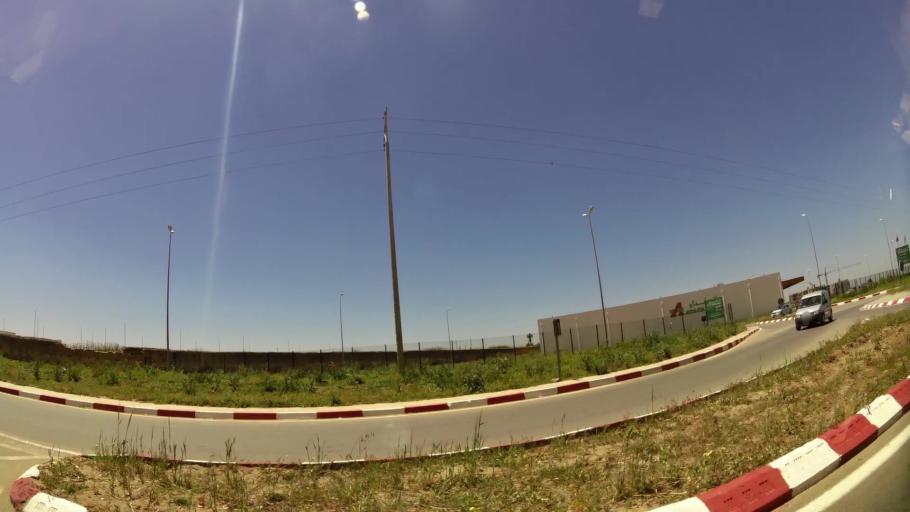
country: MA
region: Meknes-Tafilalet
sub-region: Meknes
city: Meknes
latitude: 33.8520
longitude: -5.5643
